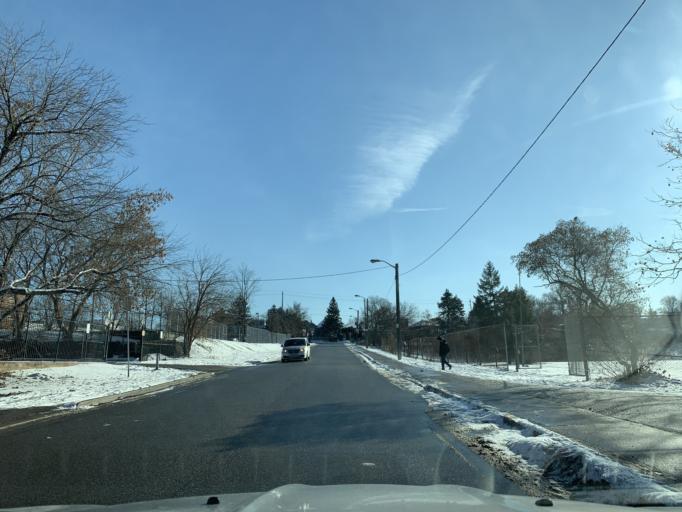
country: CA
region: Ontario
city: Toronto
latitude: 43.6816
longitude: -79.4789
